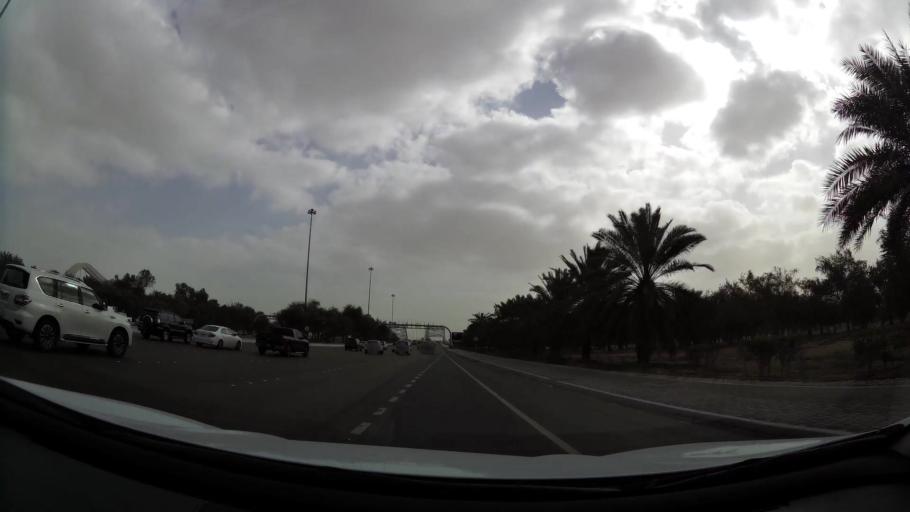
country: AE
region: Abu Dhabi
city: Abu Dhabi
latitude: 24.4197
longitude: 54.4818
